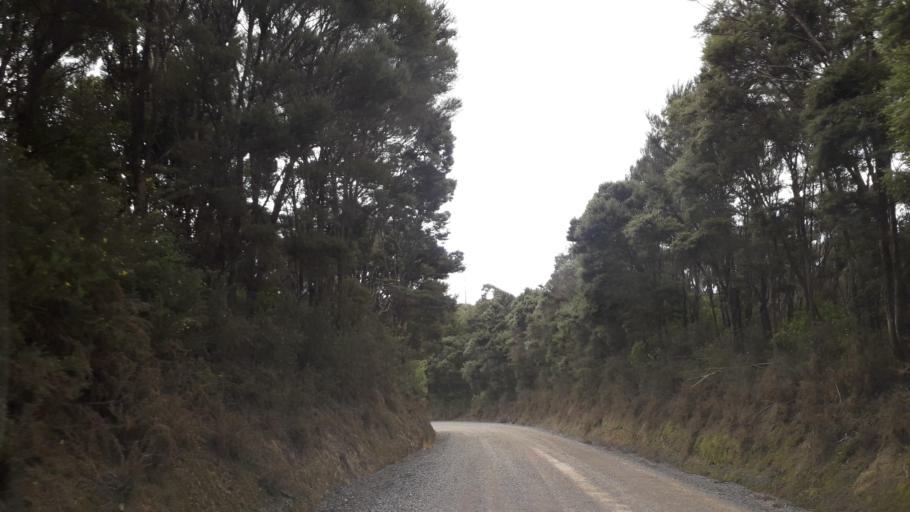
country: NZ
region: Northland
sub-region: Far North District
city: Paihia
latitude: -35.3166
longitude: 174.2261
